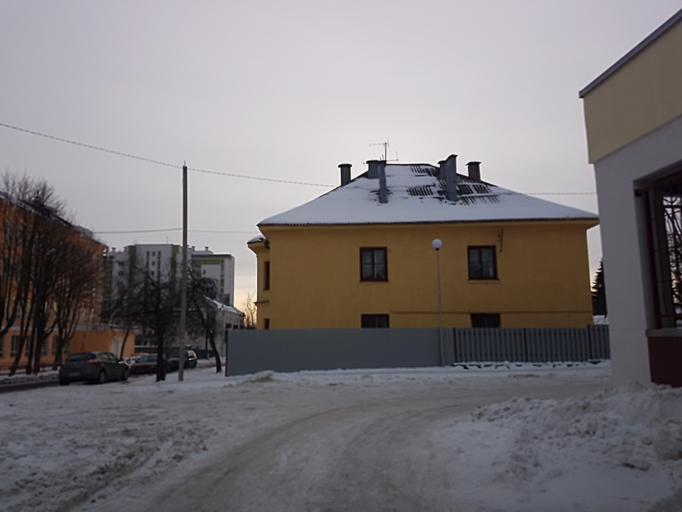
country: BY
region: Minsk
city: Minsk
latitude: 53.8848
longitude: 27.5221
